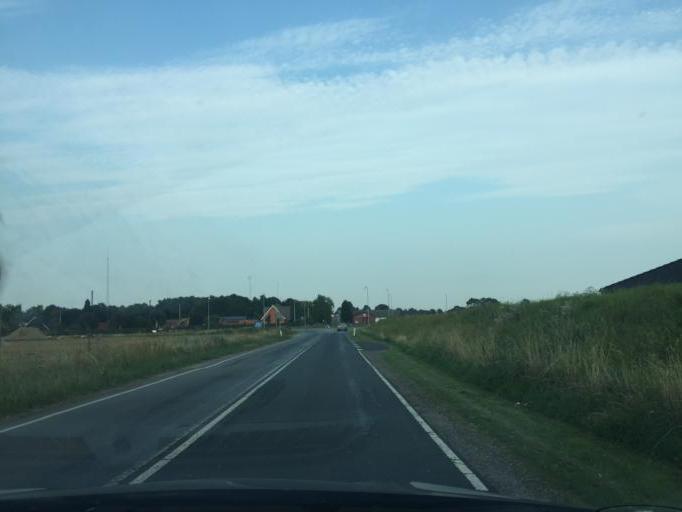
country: DK
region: South Denmark
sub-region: Kerteminde Kommune
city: Langeskov
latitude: 55.3086
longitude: 10.5929
